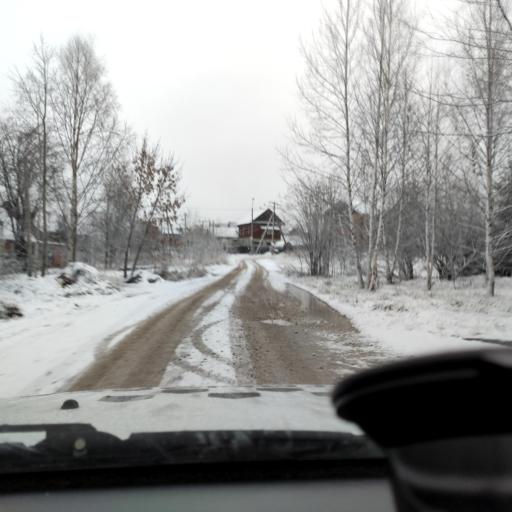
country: RU
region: Perm
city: Perm
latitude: 58.0396
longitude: 56.3624
